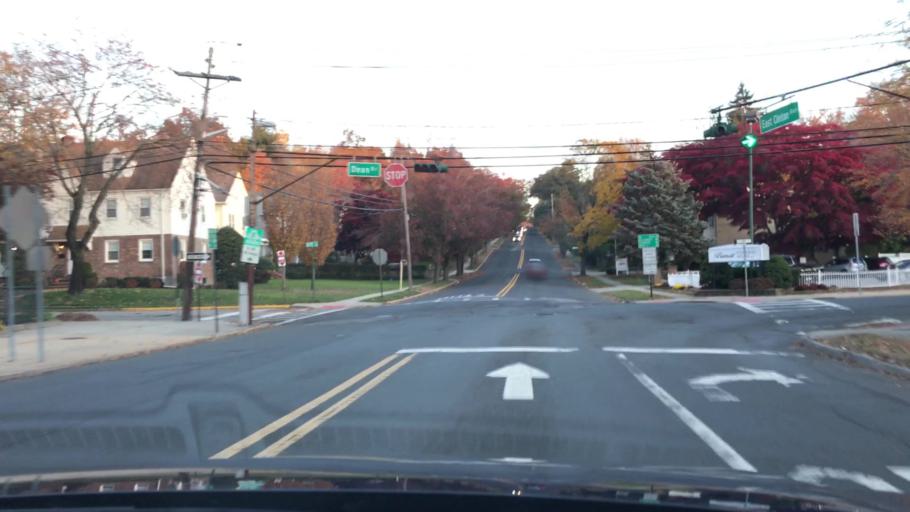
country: US
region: New Jersey
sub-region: Bergen County
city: Tenafly
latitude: 40.9233
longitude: -73.9644
